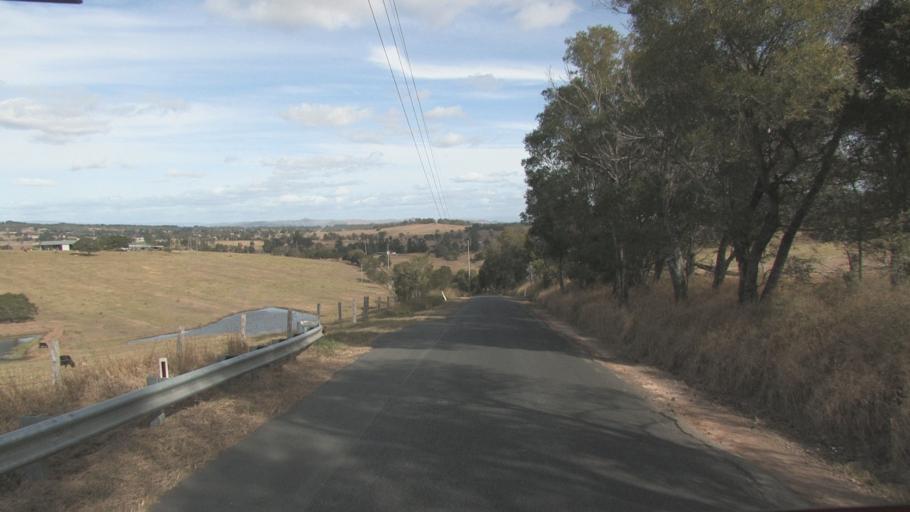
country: AU
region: Queensland
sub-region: Logan
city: Cedar Vale
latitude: -27.9052
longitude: 153.0143
